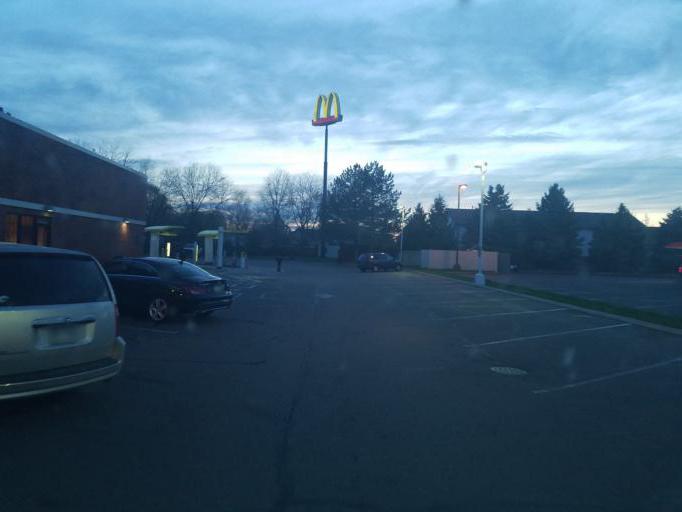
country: US
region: Michigan
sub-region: Washtenaw County
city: Milan
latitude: 42.0955
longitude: -83.6769
